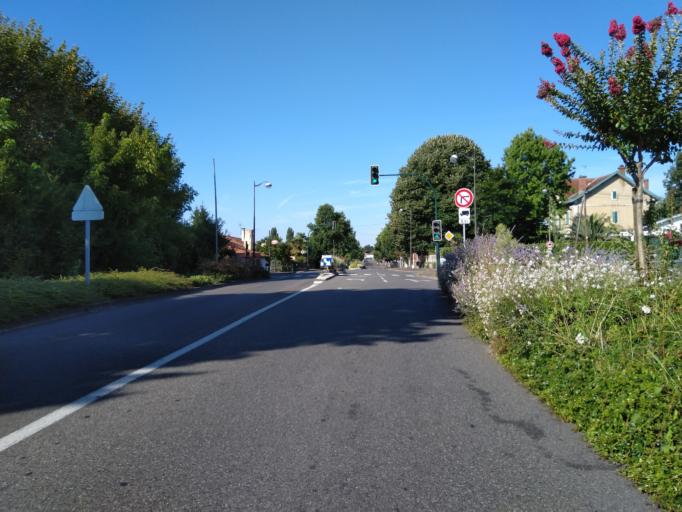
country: FR
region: Aquitaine
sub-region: Departement des Landes
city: Saint-Paul-les-Dax
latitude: 43.7271
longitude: -1.0439
